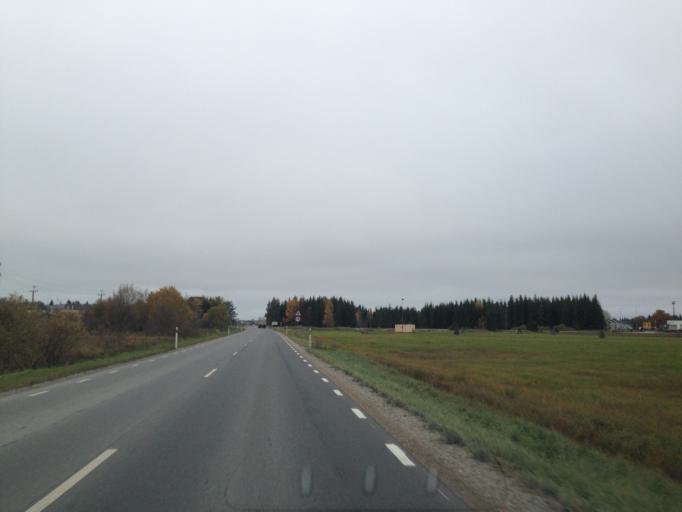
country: EE
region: Harju
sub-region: Harku vald
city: Tabasalu
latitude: 59.4050
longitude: 24.5474
